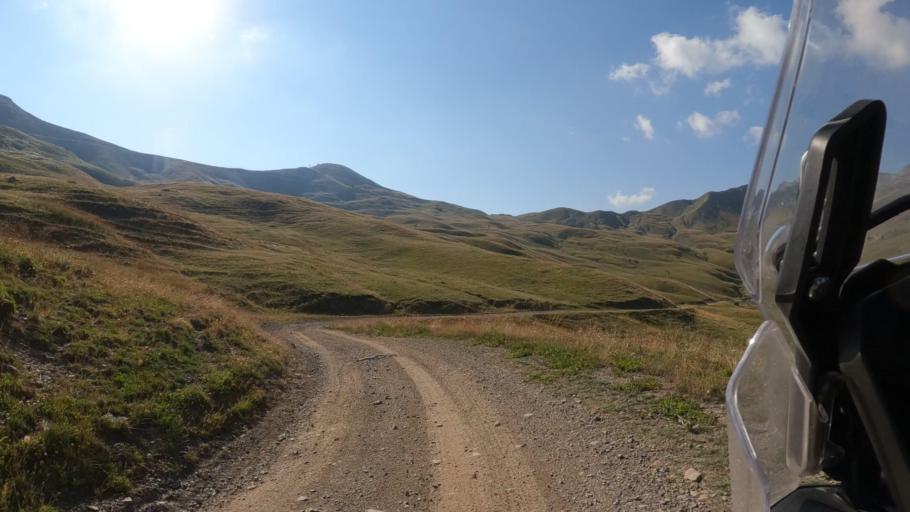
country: FR
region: Provence-Alpes-Cote d'Azur
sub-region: Departement des Hautes-Alpes
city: Guillestre
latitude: 44.5913
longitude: 6.6402
